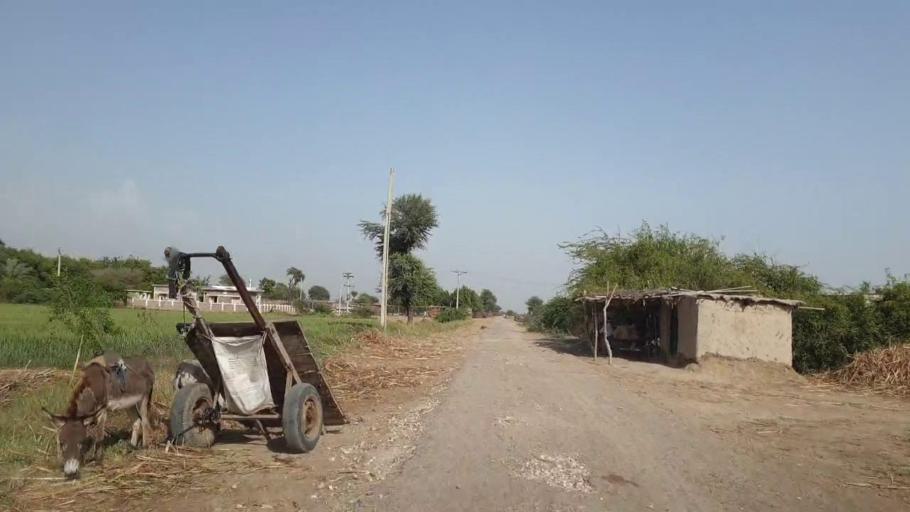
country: PK
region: Sindh
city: Tando Ghulam Ali
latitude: 25.0762
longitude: 68.8458
